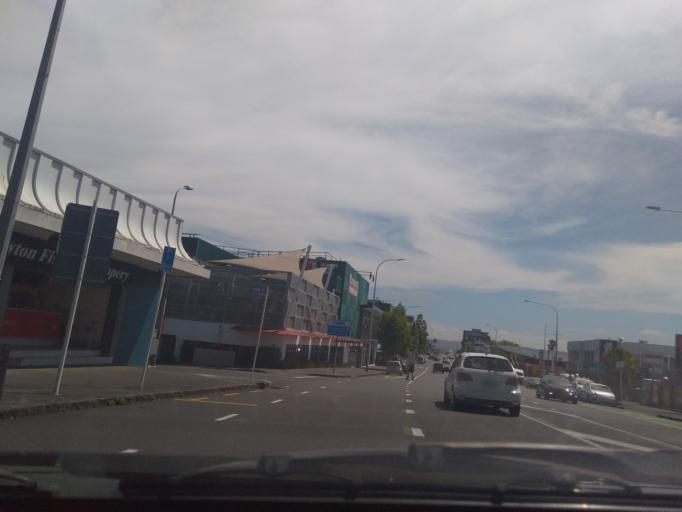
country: NZ
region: Auckland
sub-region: Auckland
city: Auckland
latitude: -36.8648
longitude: 174.7465
